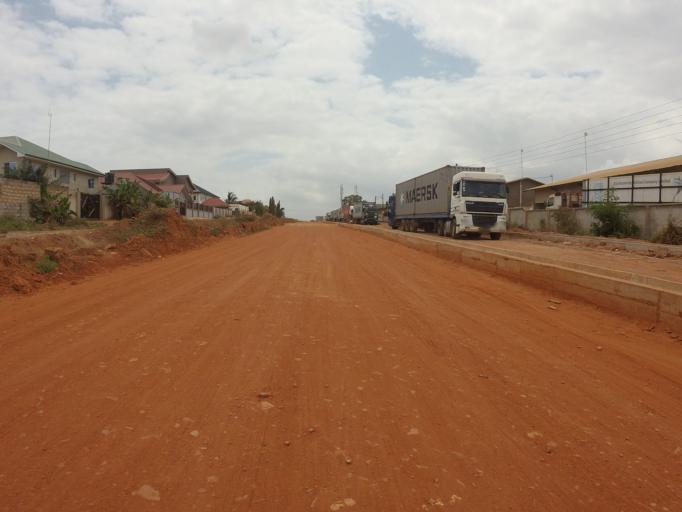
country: GH
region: Greater Accra
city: Medina Estates
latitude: 5.6288
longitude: -0.1439
